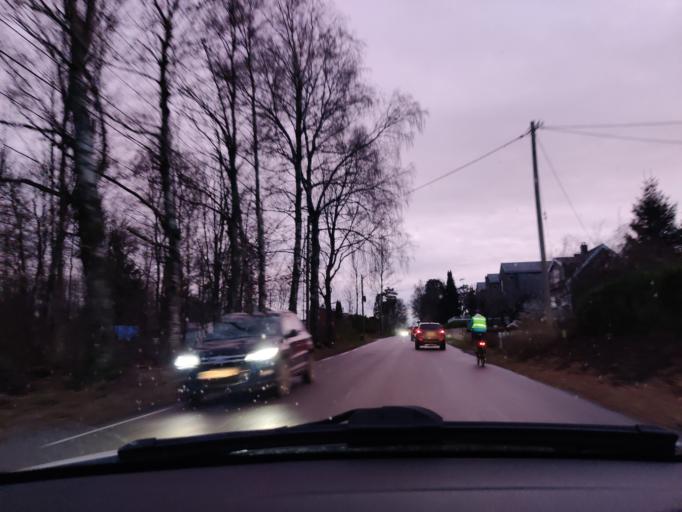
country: NO
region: Vestfold
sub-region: Tonsberg
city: Sem
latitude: 59.2682
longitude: 10.3652
